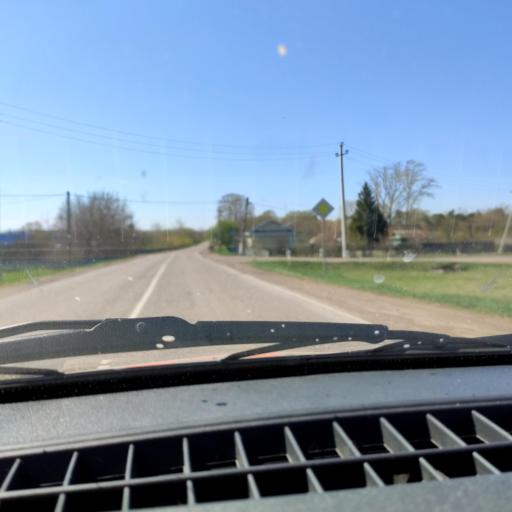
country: RU
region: Bashkortostan
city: Kushnarenkovo
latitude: 55.0532
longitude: 55.1406
